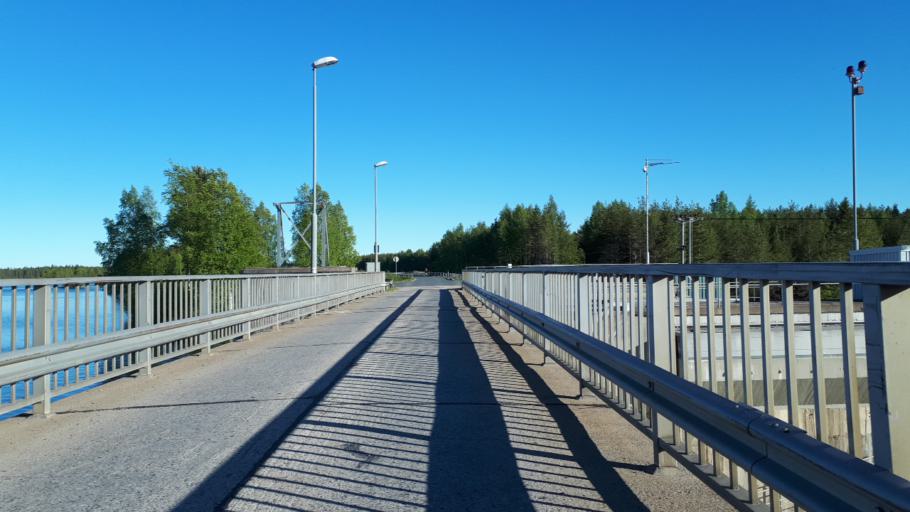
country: FI
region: Northern Ostrobothnia
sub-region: Oulunkaari
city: Ii
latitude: 65.3251
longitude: 25.5241
